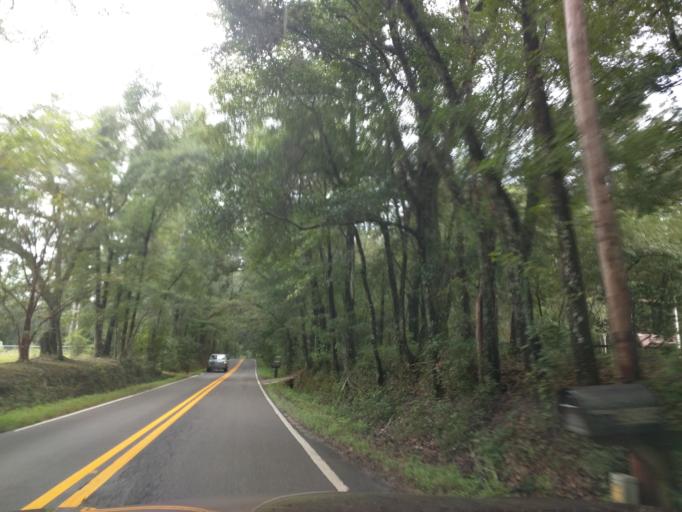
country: US
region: Florida
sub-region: Leon County
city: Tallahassee
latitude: 30.5208
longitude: -84.1226
